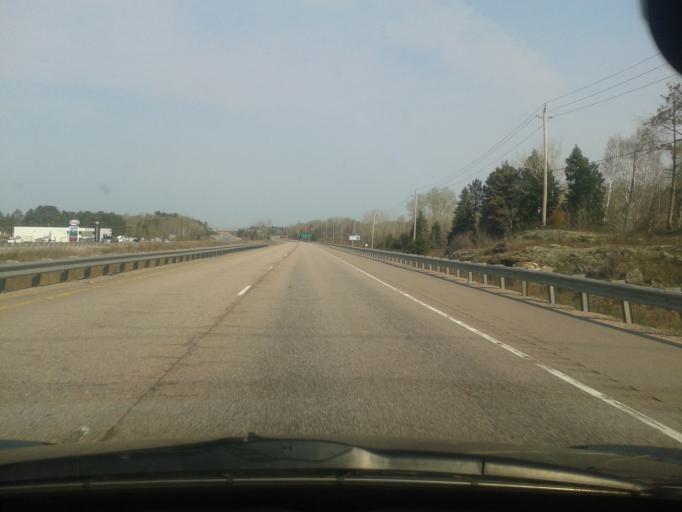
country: CA
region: Ontario
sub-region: Nipissing District
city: North Bay
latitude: 46.2579
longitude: -79.3813
